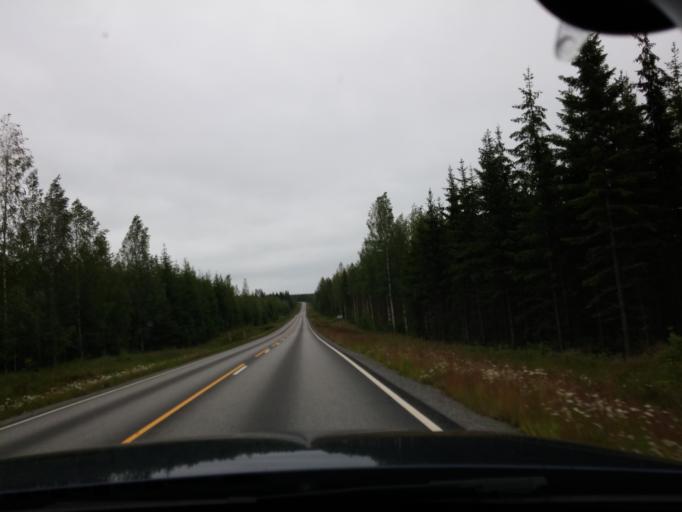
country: FI
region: Central Finland
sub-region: Saarijaervi-Viitasaari
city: Saarijaervi
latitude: 62.6793
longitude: 25.1968
